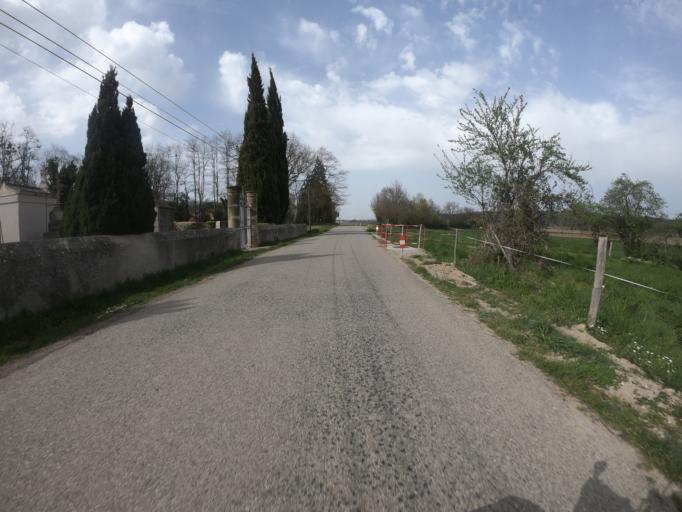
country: FR
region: Midi-Pyrenees
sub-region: Departement de l'Ariege
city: La Tour-du-Crieu
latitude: 43.1138
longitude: 1.7229
